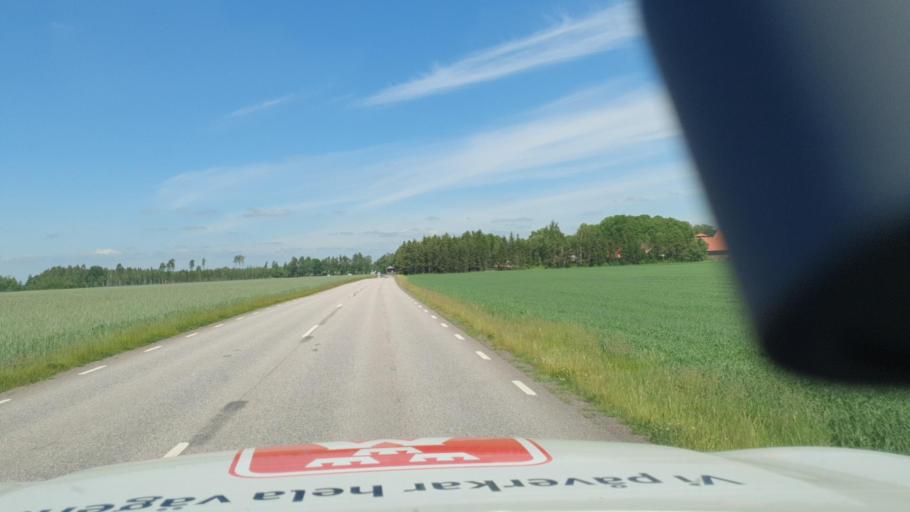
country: SE
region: Vaestra Goetaland
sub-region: Vara Kommun
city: Vara
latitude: 58.2254
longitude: 13.0020
